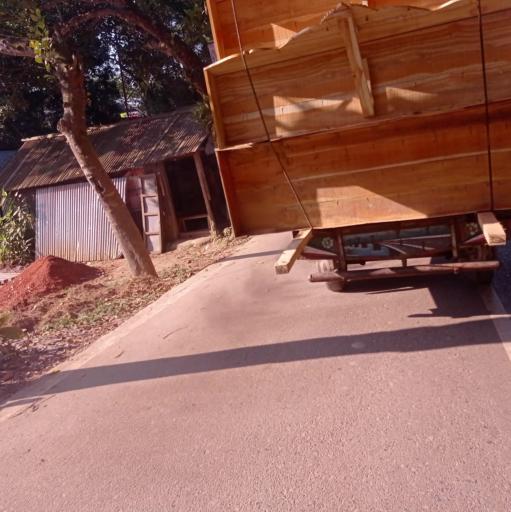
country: BD
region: Dhaka
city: Bhairab Bazar
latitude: 24.1086
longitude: 90.8506
